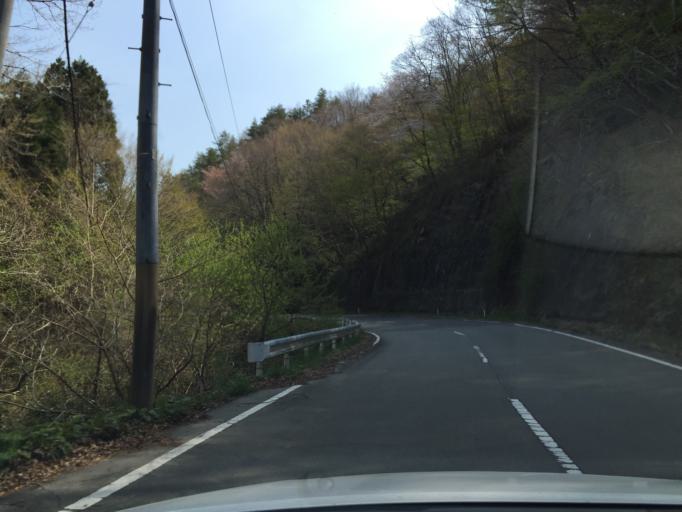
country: JP
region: Fukushima
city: Iwaki
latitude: 37.2377
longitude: 140.8462
